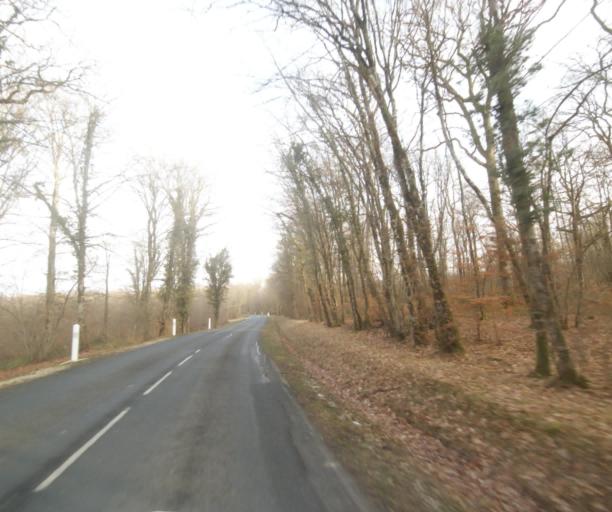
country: FR
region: Champagne-Ardenne
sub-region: Departement de la Marne
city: Sermaize-les-Bains
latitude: 48.7536
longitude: 4.9005
